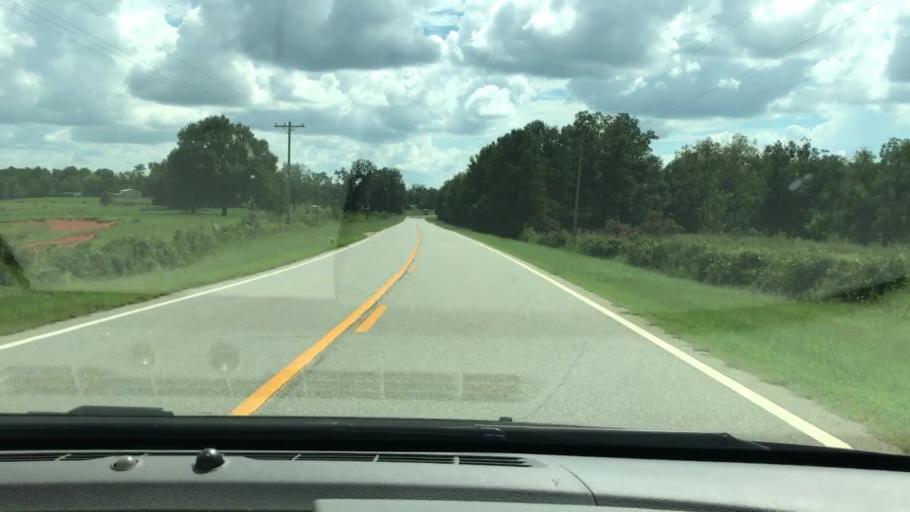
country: US
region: Georgia
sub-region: Quitman County
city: Georgetown
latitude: 31.8992
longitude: -85.0800
